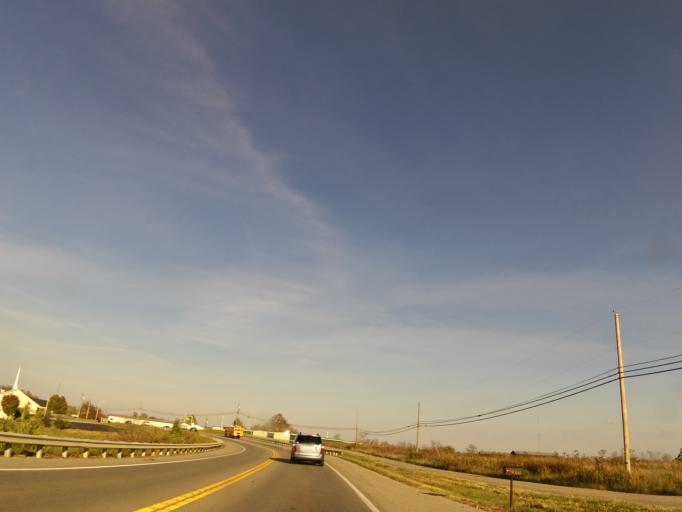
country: US
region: Kentucky
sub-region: Garrard County
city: Lancaster
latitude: 37.6042
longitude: -84.5837
